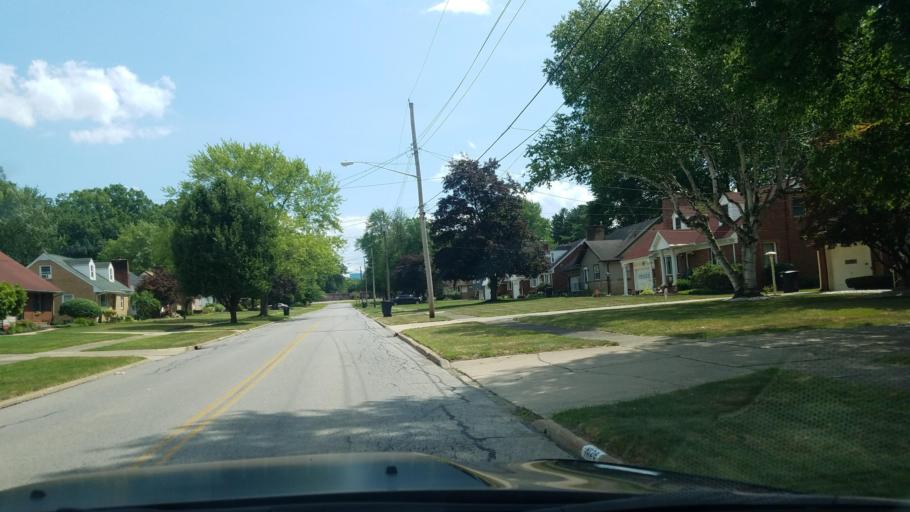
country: US
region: Ohio
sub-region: Trumbull County
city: Bolindale
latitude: 41.2275
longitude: -80.7783
